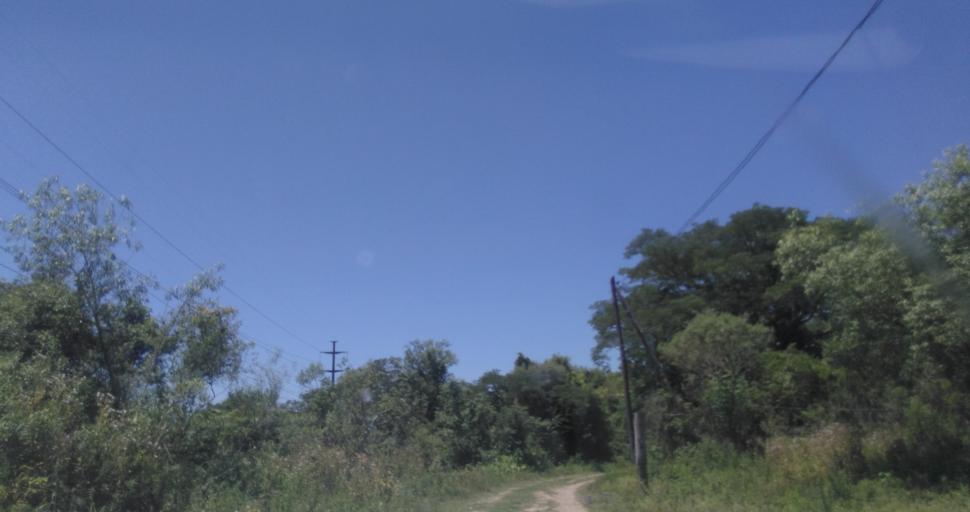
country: AR
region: Chaco
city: Fontana
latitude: -27.4116
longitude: -59.0155
